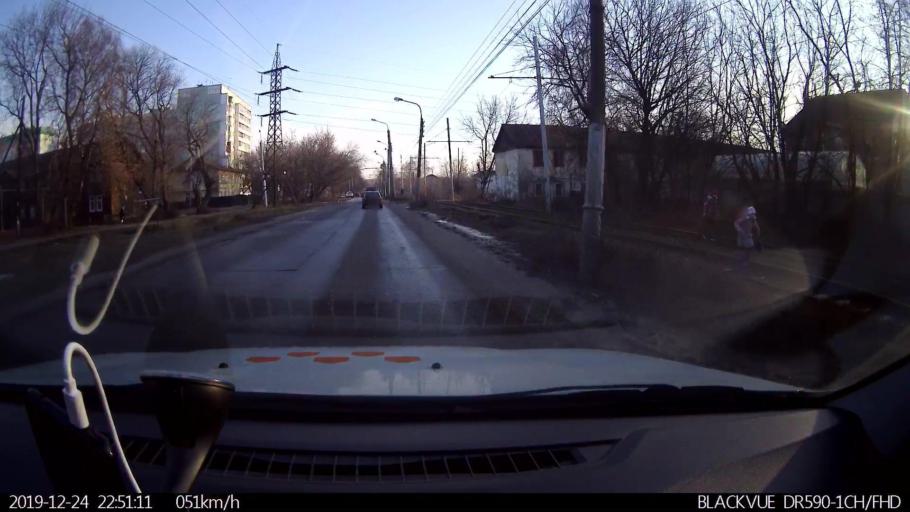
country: RU
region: Nizjnij Novgorod
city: Nizhniy Novgorod
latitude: 56.2888
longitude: 43.9074
